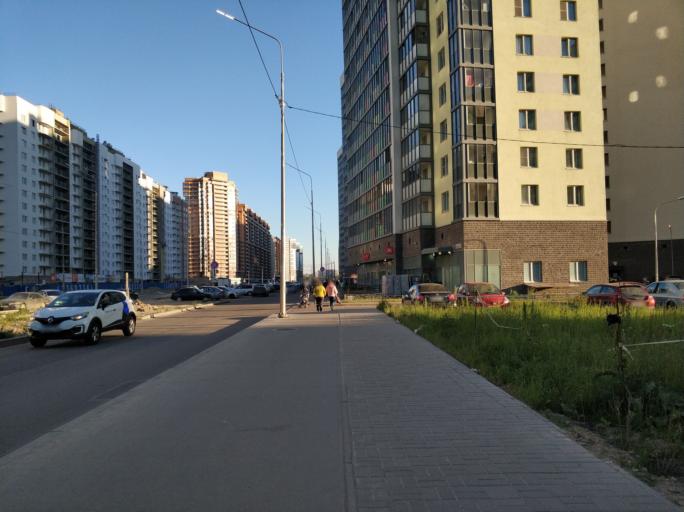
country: RU
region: Leningrad
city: Murino
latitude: 60.0606
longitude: 30.4308
